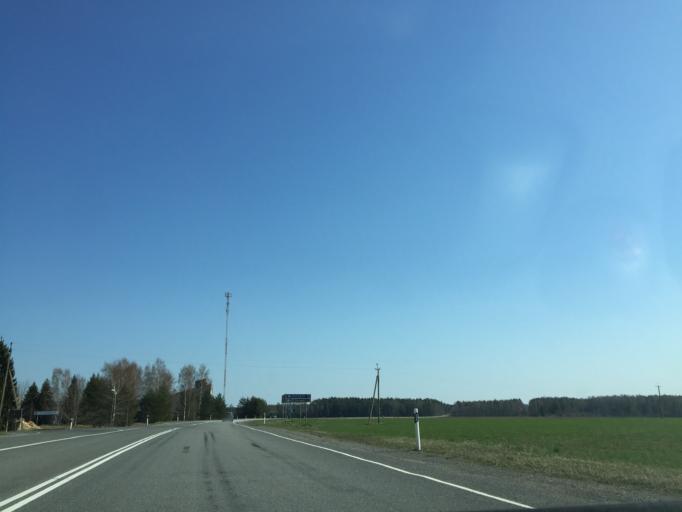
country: EE
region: Tartu
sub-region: Tartu linn
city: Tartu
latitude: 58.5090
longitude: 26.8898
